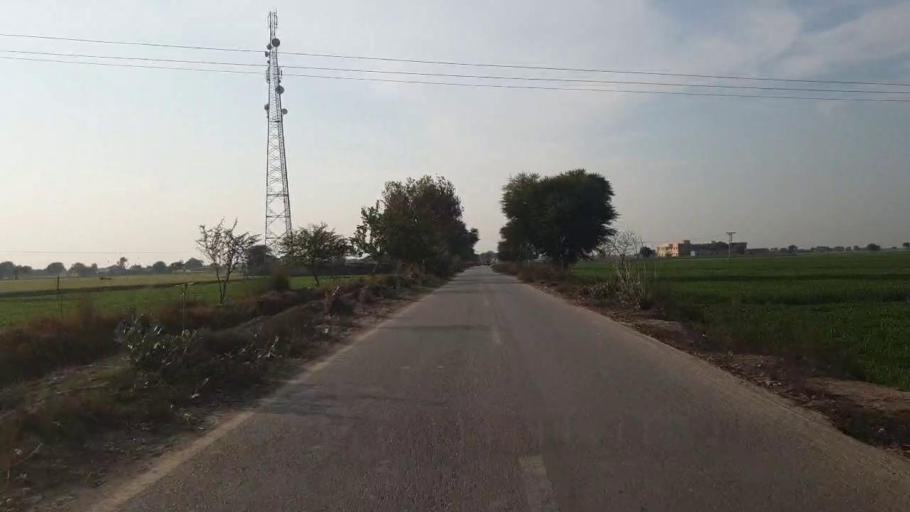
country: PK
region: Sindh
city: Shahpur Chakar
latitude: 26.1610
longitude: 68.6347
